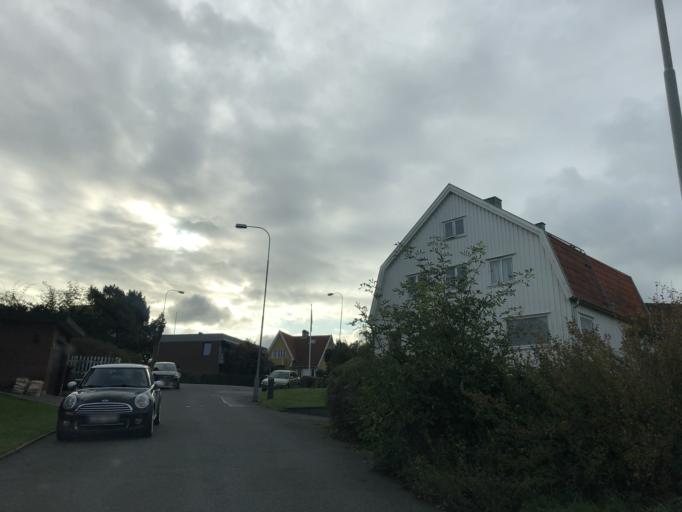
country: SE
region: Vaestra Goetaland
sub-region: Goteborg
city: Majorna
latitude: 57.6772
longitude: 11.8685
